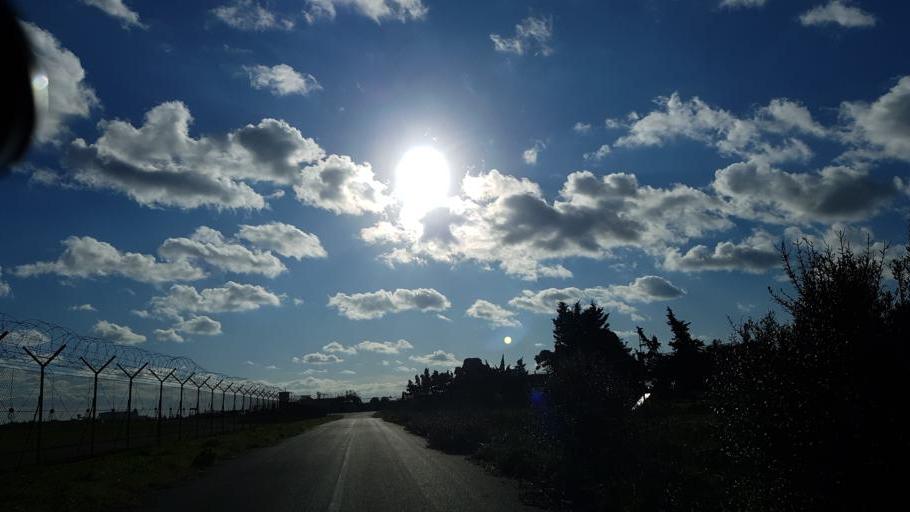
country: IT
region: Apulia
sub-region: Provincia di Brindisi
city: Materdomini
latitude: 40.6615
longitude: 17.9401
